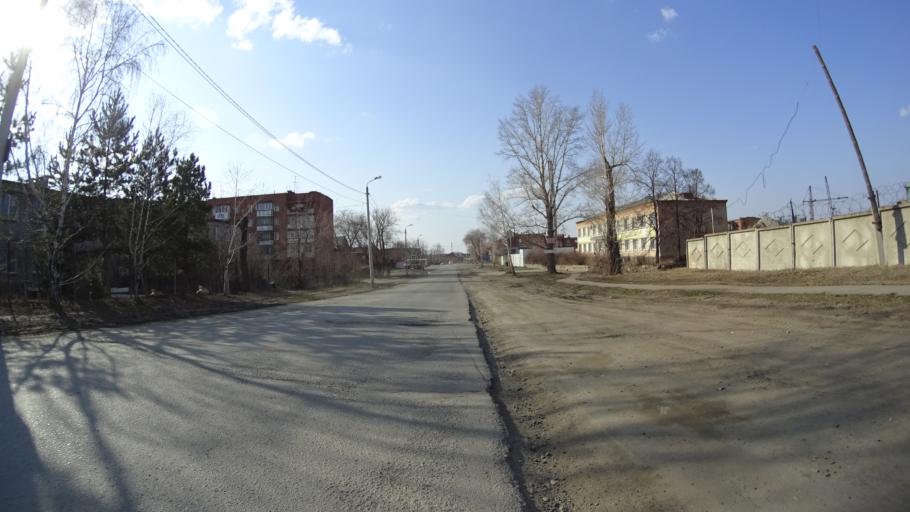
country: RU
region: Chelyabinsk
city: Novosineglazovskiy
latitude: 55.1058
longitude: 61.3386
